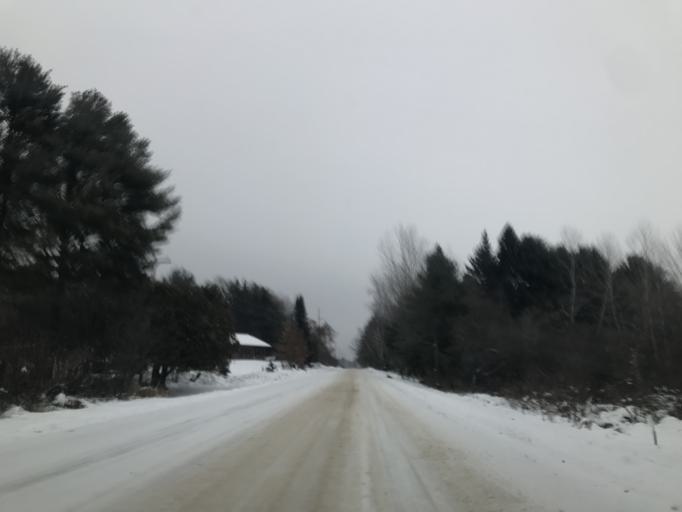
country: US
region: Wisconsin
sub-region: Marinette County
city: Peshtigo
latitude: 45.0640
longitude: -87.7384
